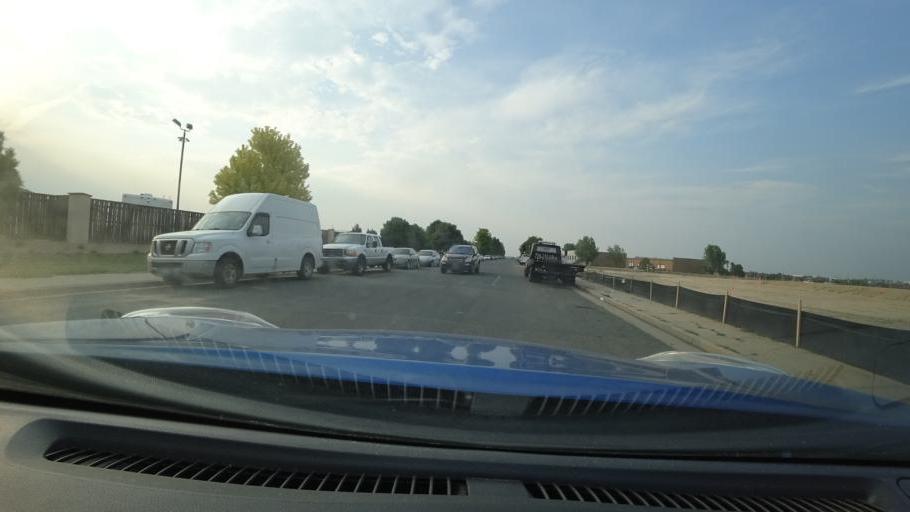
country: US
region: Colorado
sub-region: Adams County
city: Aurora
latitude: 39.7294
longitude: -104.7832
